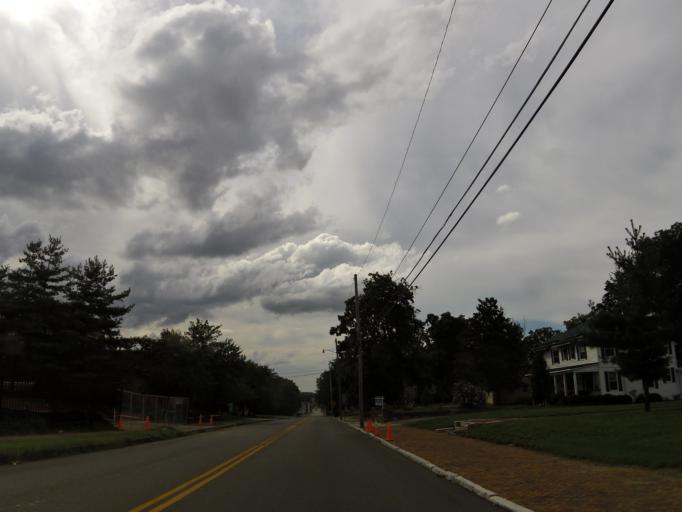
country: US
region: Kentucky
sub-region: Christian County
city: Hopkinsville
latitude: 36.8632
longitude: -87.4805
